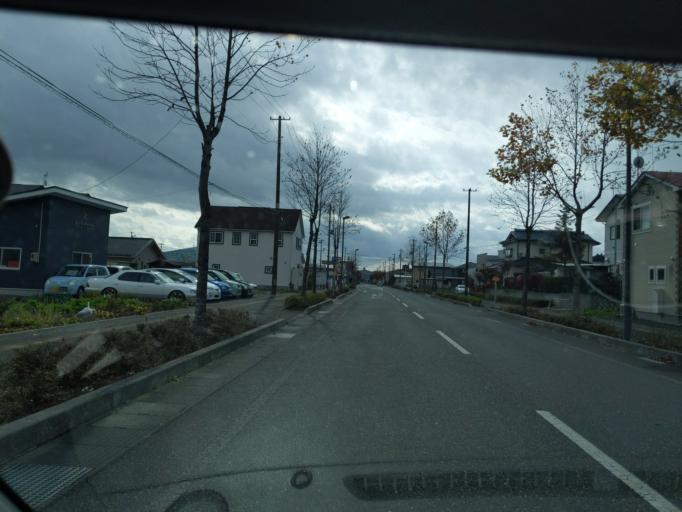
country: JP
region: Iwate
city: Mizusawa
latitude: 39.0567
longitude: 141.1256
